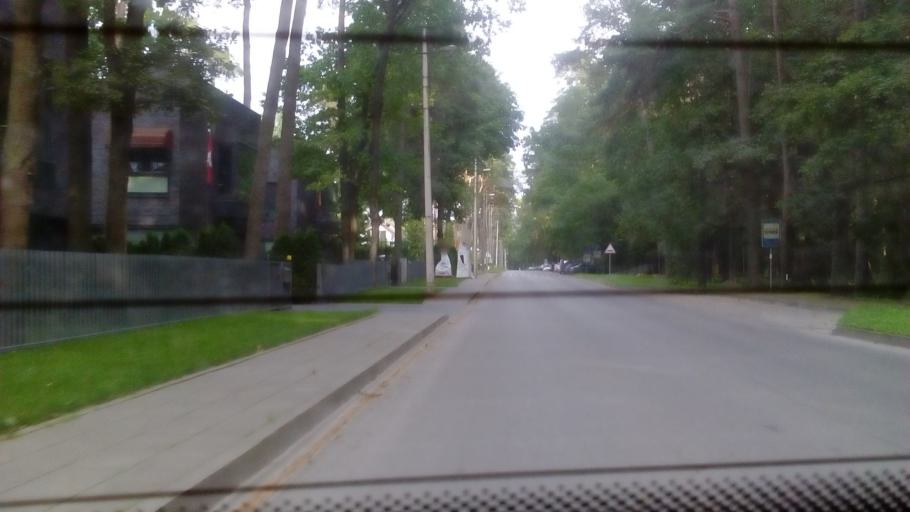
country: LT
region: Alytaus apskritis
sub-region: Alytus
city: Alytus
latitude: 54.3942
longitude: 24.0605
